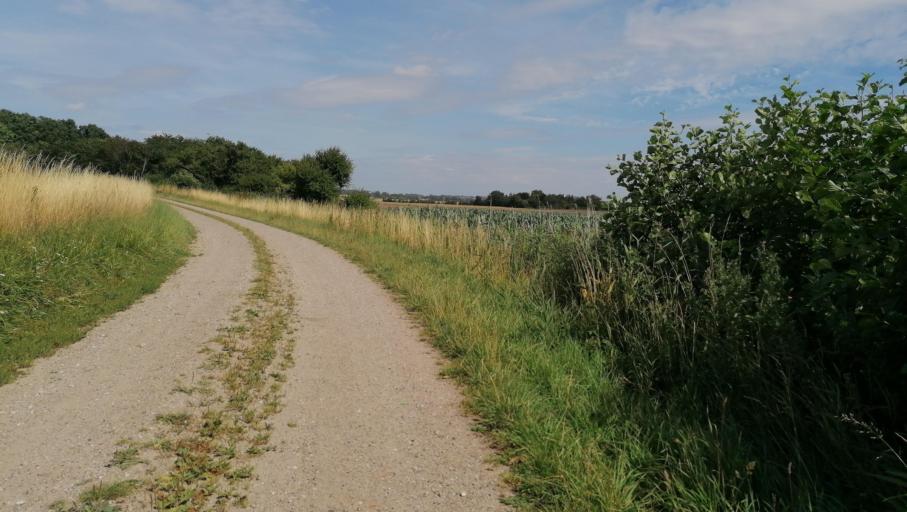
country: DK
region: Zealand
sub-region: Odsherred Kommune
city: Horve
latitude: 55.7895
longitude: 11.4250
